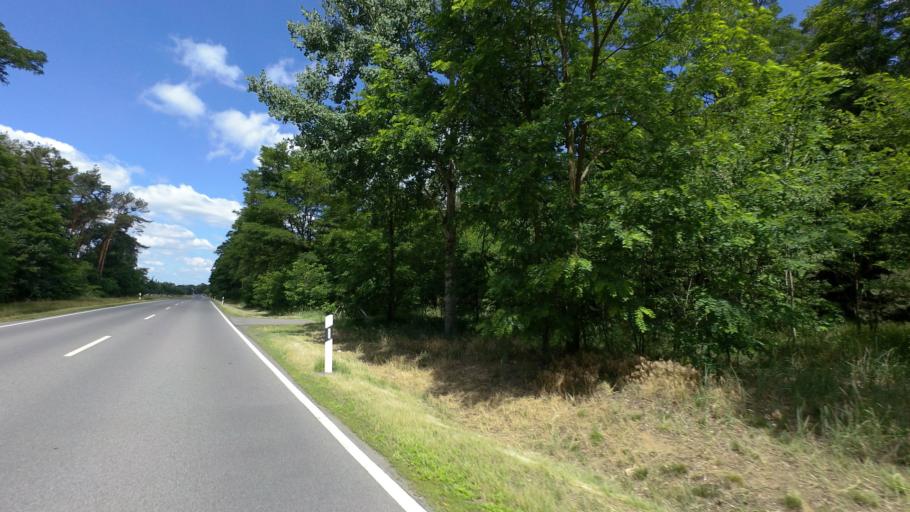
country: DE
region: Brandenburg
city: Finsterwalde
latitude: 51.6261
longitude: 13.7802
